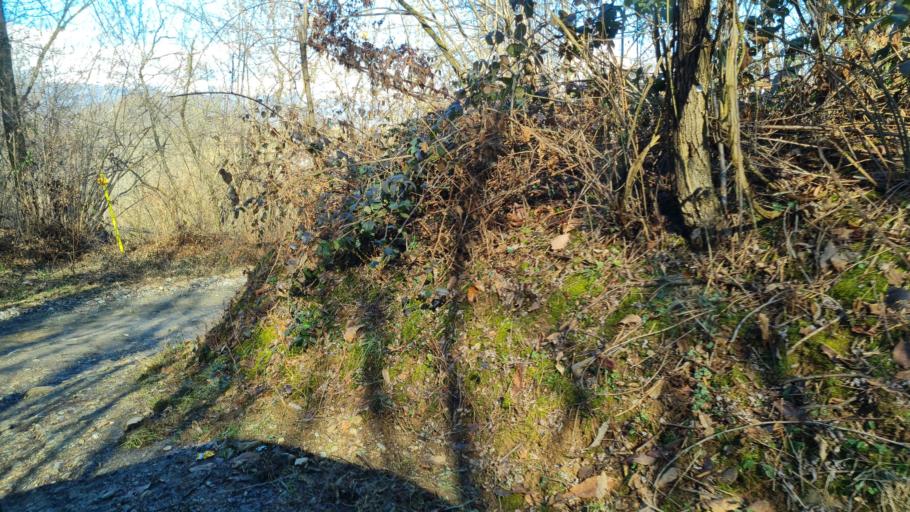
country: IT
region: Piedmont
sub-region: Provincia di Biella
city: Zubiena
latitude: 45.5004
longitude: 7.9995
